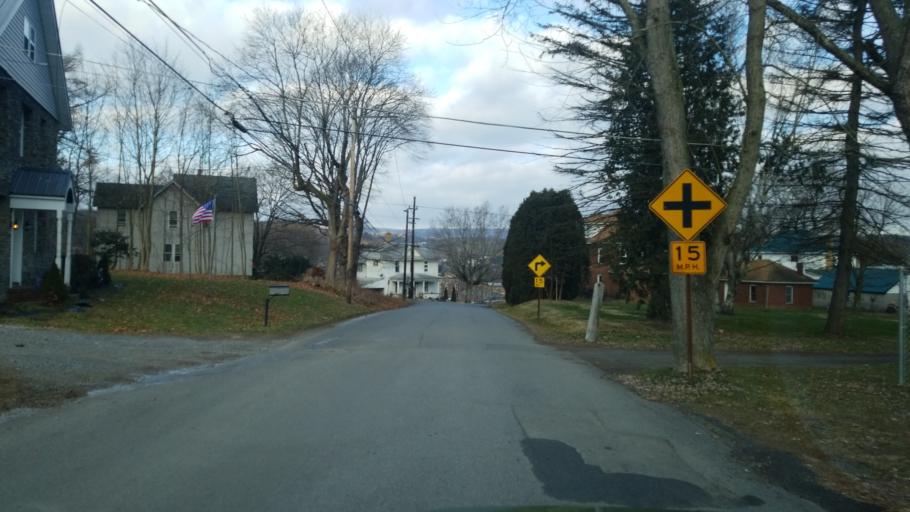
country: US
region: Pennsylvania
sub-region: Clearfield County
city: Clearfield
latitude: 41.0188
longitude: -78.4312
